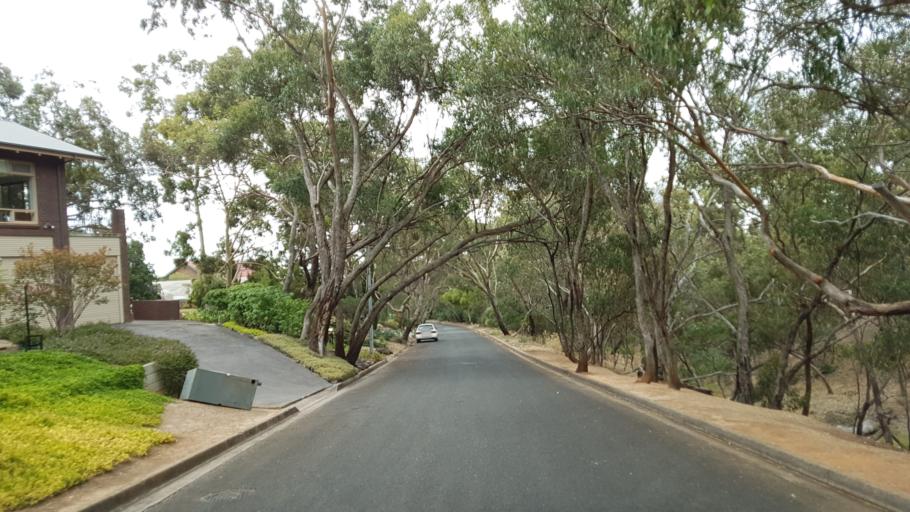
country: AU
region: South Australia
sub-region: Mitcham
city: Clapham
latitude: -35.0060
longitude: 138.5954
